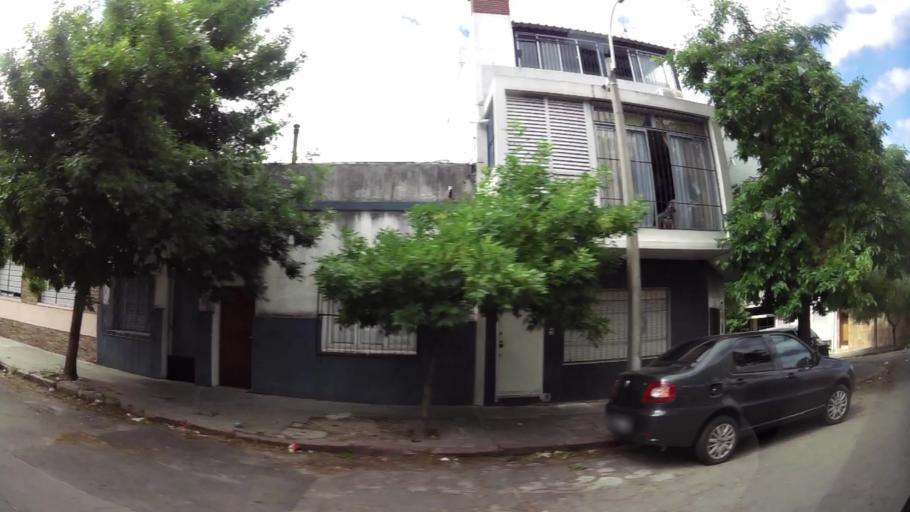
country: UY
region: Montevideo
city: Montevideo
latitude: -34.8803
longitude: -56.1728
